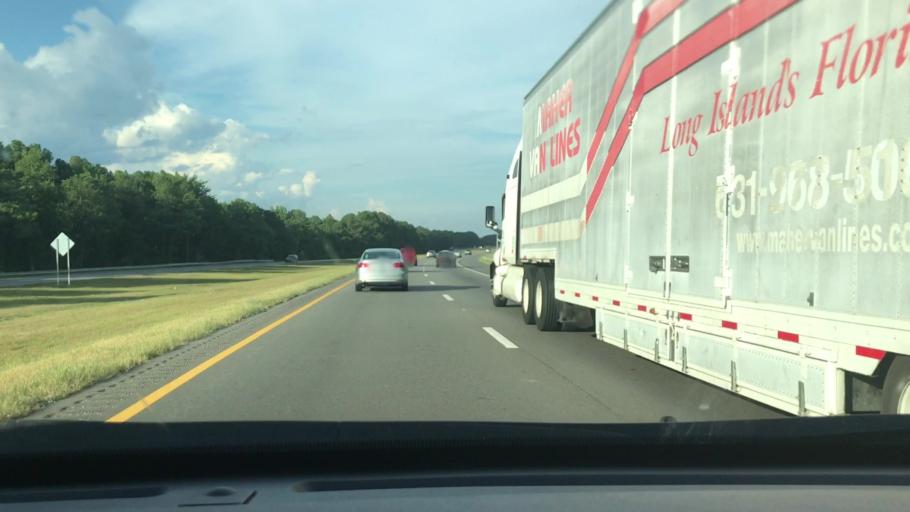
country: US
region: North Carolina
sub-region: Cumberland County
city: Hope Mills
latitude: 34.9332
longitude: -78.9354
